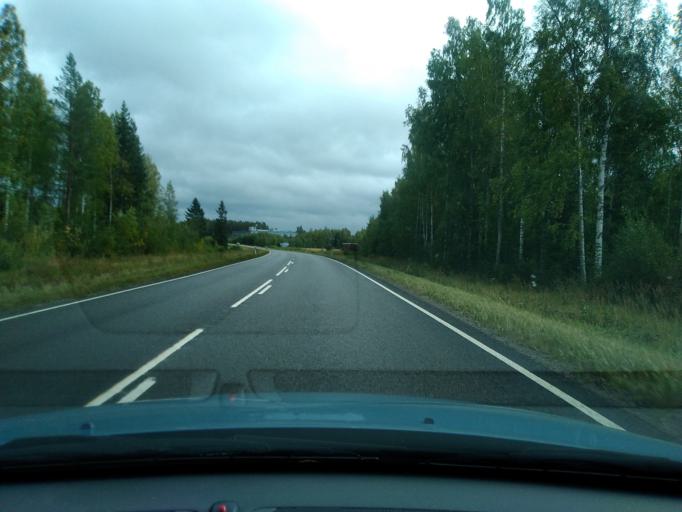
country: FI
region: Central Finland
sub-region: Saarijaervi-Viitasaari
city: Saarijaervi
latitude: 62.6774
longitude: 25.3711
